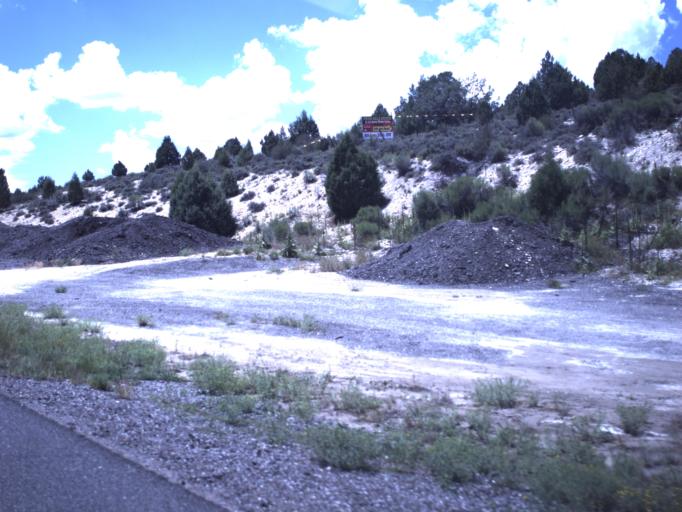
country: US
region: Utah
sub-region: Garfield County
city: Panguitch
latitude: 37.6065
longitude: -112.4677
